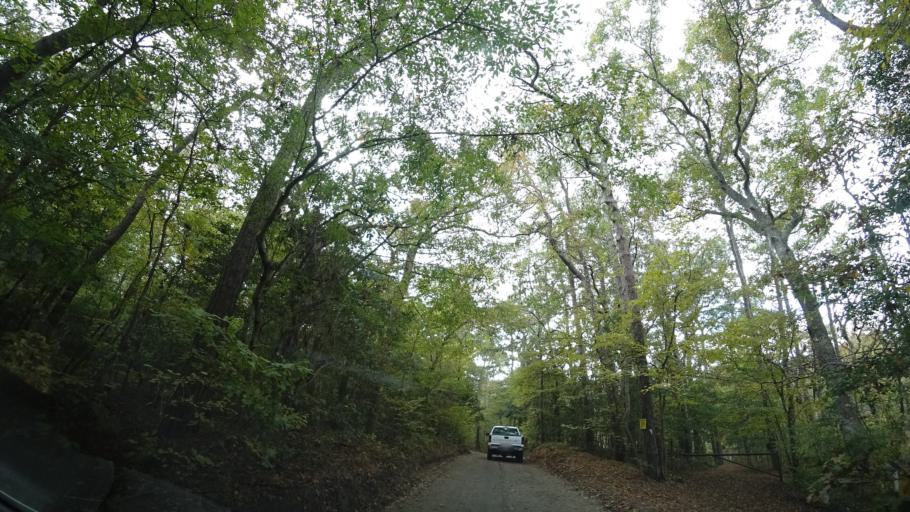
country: US
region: North Carolina
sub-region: Dare County
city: Kill Devil Hills
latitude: 35.9988
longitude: -75.6653
